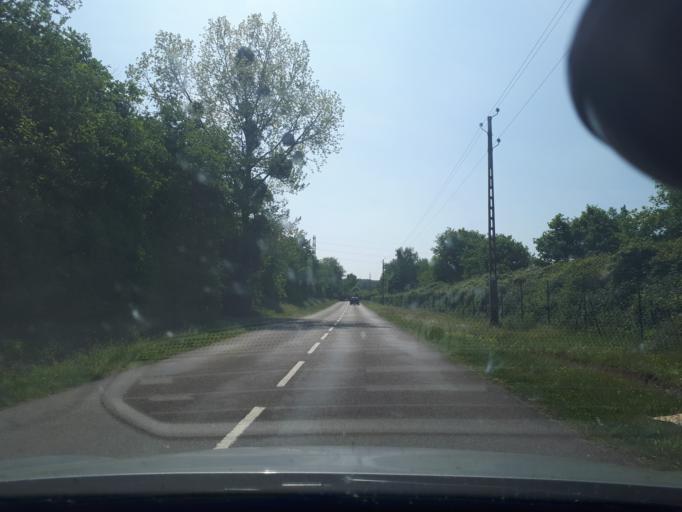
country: FR
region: Pays de la Loire
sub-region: Departement de la Sarthe
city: Montfort-le-Gesnois
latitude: 48.0427
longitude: 0.4213
